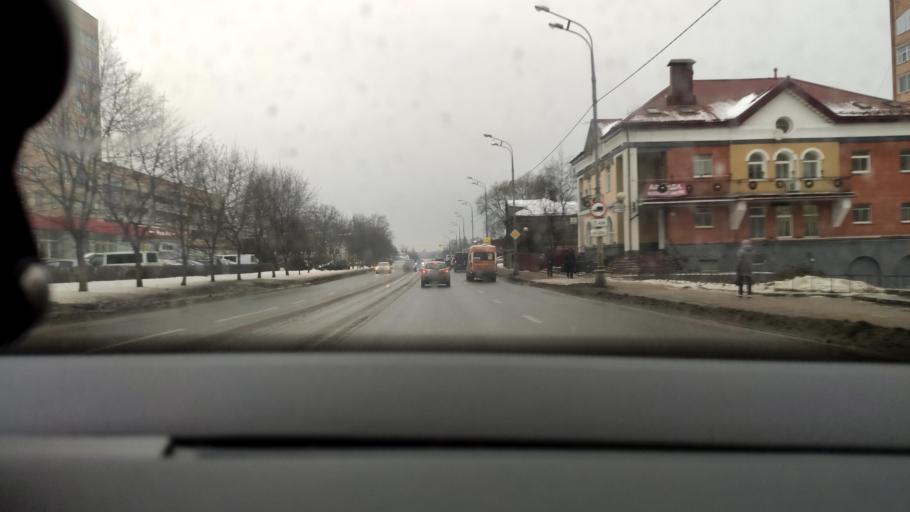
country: RU
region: Moskovskaya
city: Sergiyev Posad
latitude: 56.2976
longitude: 38.1287
